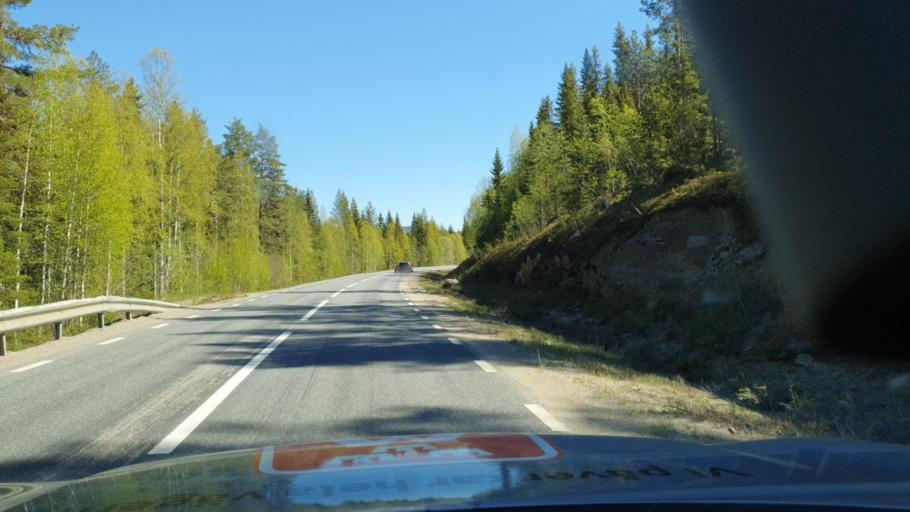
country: SE
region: Vaesternorrland
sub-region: OErnskoeldsviks Kommun
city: Bredbyn
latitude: 63.8050
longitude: 18.4867
